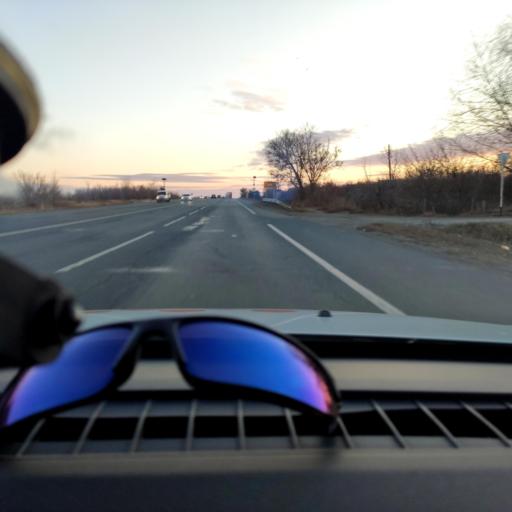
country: RU
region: Samara
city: Novokuybyshevsk
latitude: 53.0753
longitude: 50.0360
